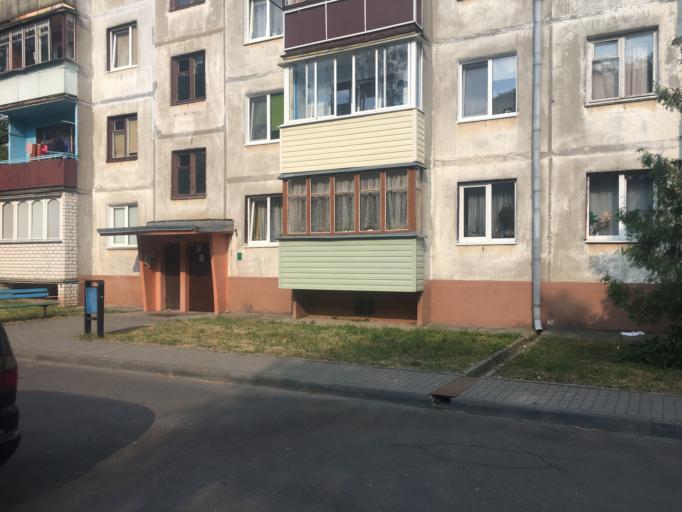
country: BY
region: Grodnenskaya
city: Hrodna
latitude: 53.6674
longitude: 23.8036
